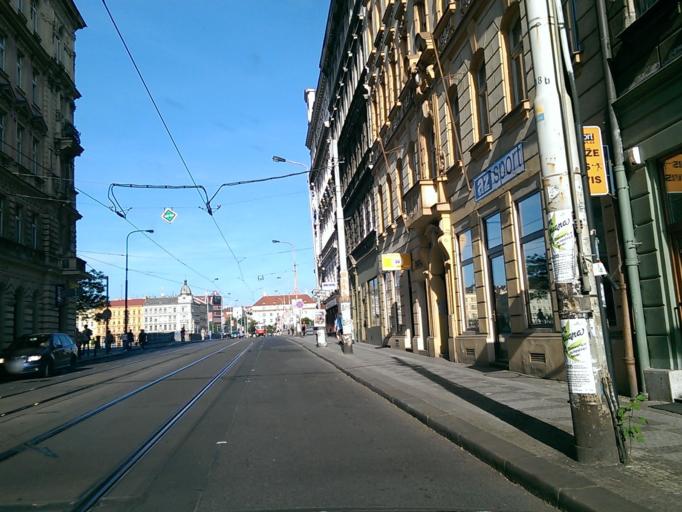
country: CZ
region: Praha
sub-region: Praha 2
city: Vysehrad
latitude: 50.0725
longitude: 14.4093
